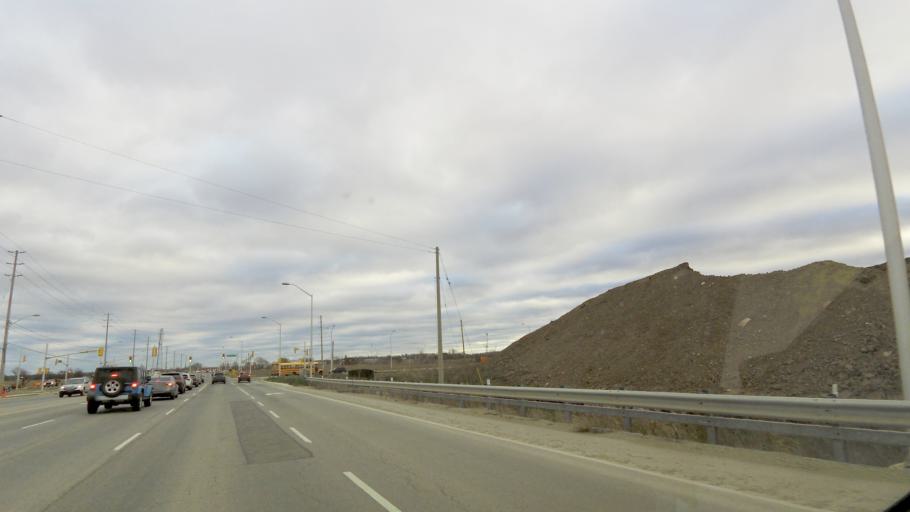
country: CA
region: Ontario
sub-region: Halton
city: Milton
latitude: 43.4874
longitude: -79.8359
